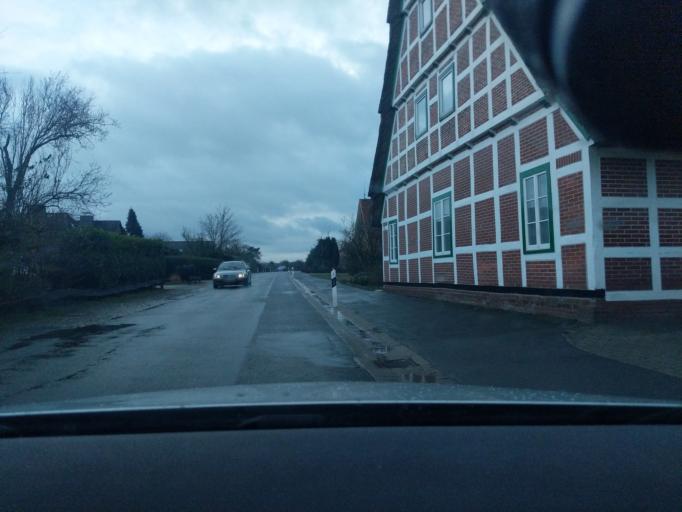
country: DE
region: Lower Saxony
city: Jork
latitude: 53.5330
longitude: 9.6524
